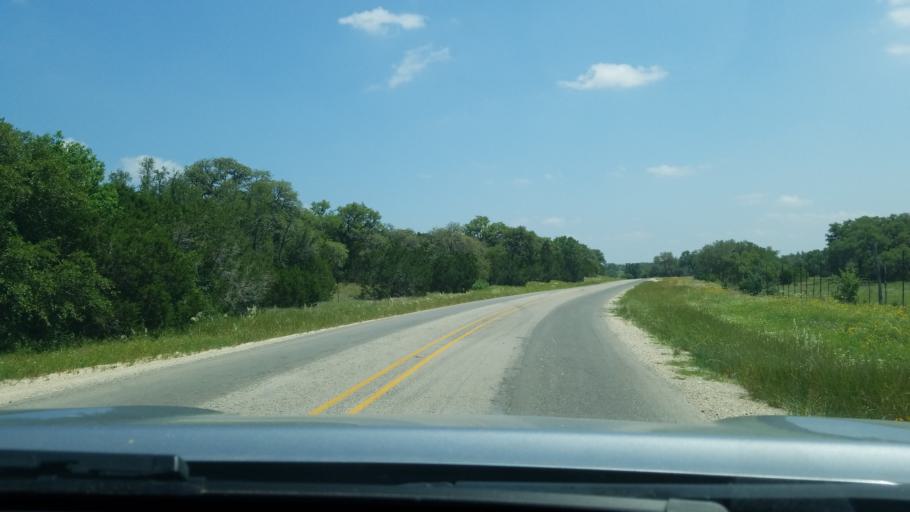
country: US
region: Texas
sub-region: Blanco County
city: Blanco
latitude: 29.9821
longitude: -98.5493
